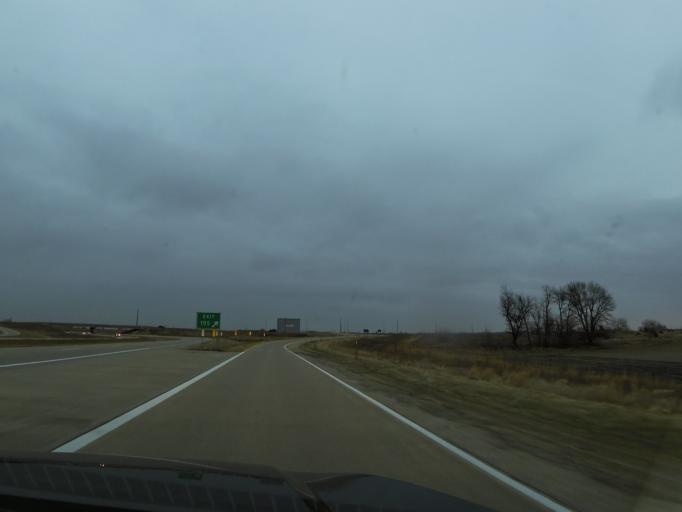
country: US
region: Iowa
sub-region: Bremer County
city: Waverly
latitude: 42.6449
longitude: -92.4513
